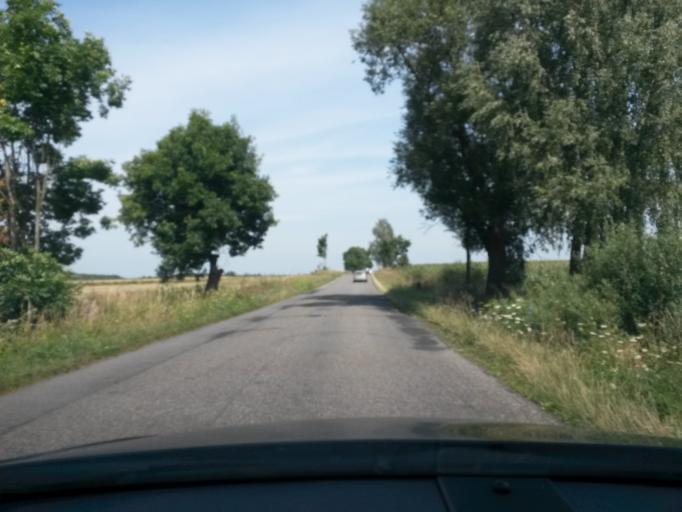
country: PL
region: Lower Silesian Voivodeship
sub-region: Powiat legnicki
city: Prochowice
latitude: 51.2493
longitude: 16.3629
